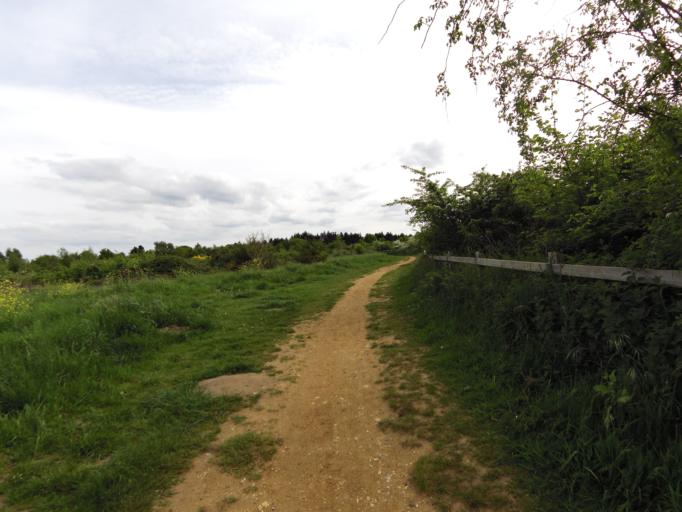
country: GB
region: England
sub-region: Suffolk
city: Ipswich
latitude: 52.0249
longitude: 1.1907
